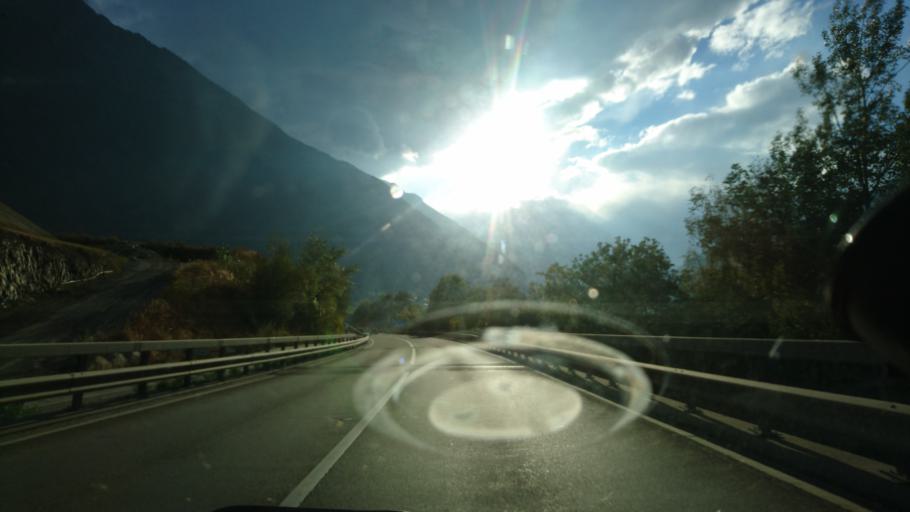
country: CH
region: Valais
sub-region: Brig District
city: Naters
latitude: 46.3147
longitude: 8.0045
